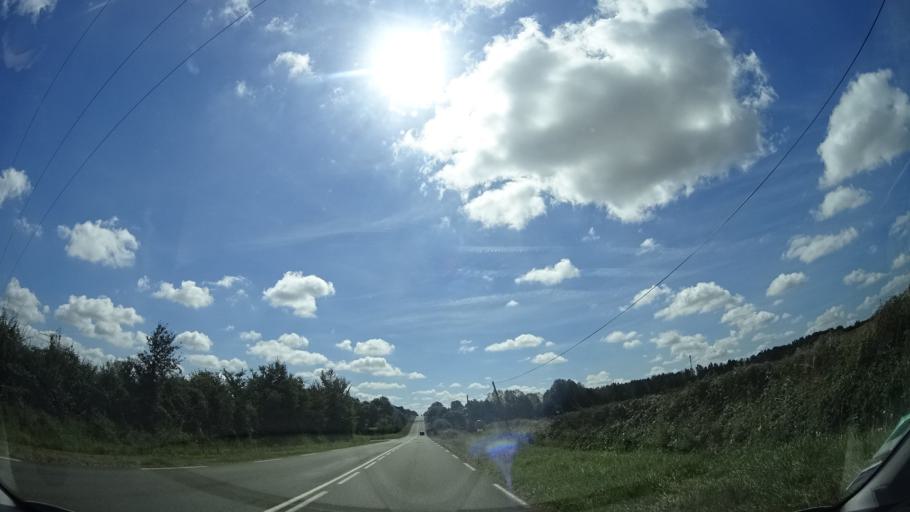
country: FR
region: Pays de la Loire
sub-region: Departement de la Mayenne
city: Meslay-du-Maine
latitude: 47.9143
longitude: -0.4650
